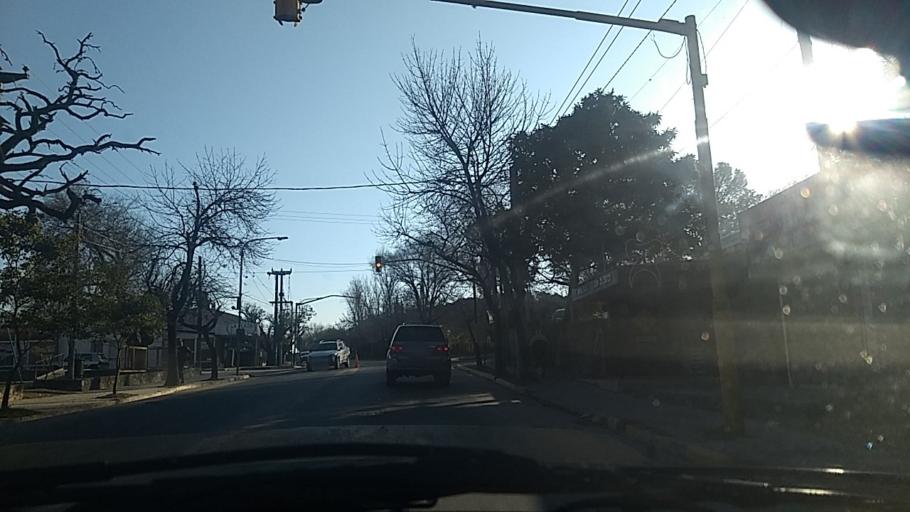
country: AR
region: Cordoba
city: Salsipuedes
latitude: -31.1361
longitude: -64.2963
